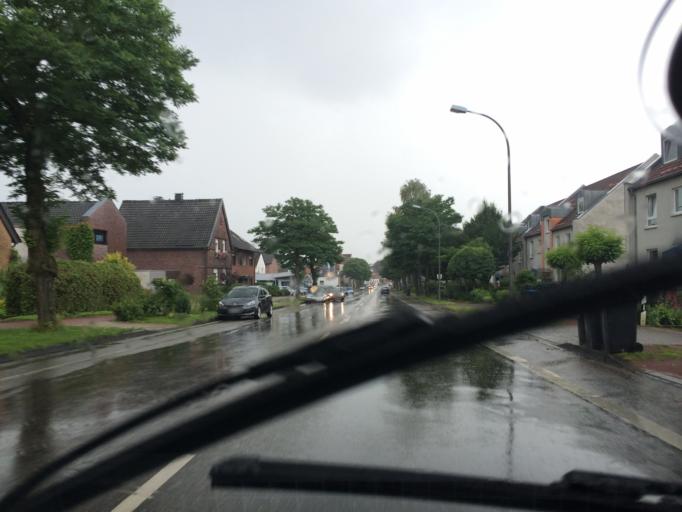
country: DE
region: North Rhine-Westphalia
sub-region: Regierungsbezirk Munster
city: Haltern
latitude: 51.7495
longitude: 7.1919
